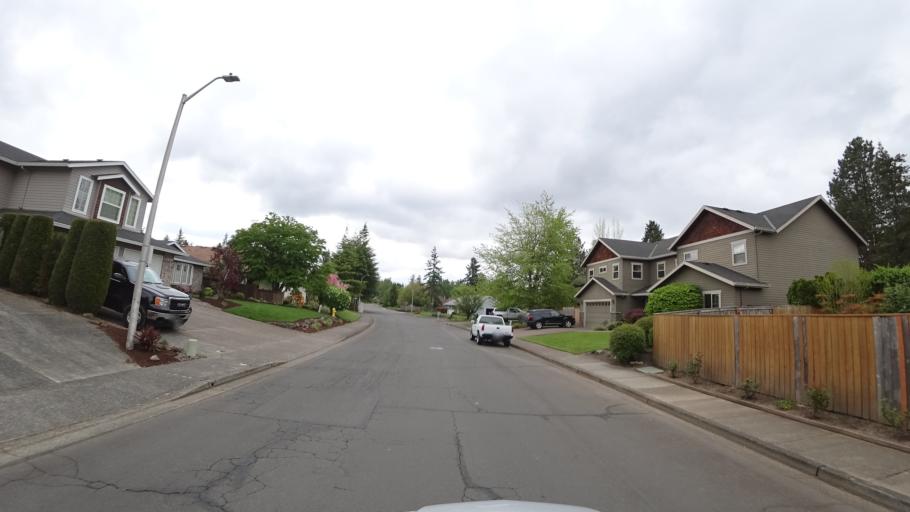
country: US
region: Oregon
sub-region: Washington County
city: Hillsboro
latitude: 45.5393
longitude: -122.9842
